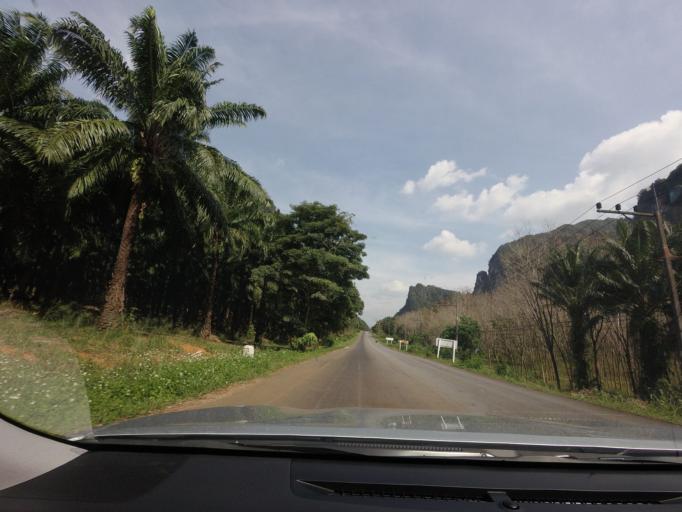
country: TH
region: Phangnga
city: Ban Ao Nang
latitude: 8.1465
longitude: 98.8141
